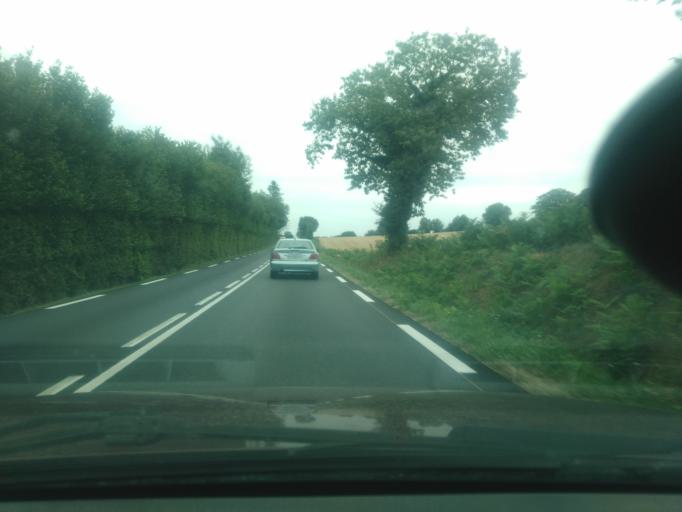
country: FR
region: Poitou-Charentes
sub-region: Departement des Deux-Sevres
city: Secondigny
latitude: 46.6156
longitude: -0.4467
